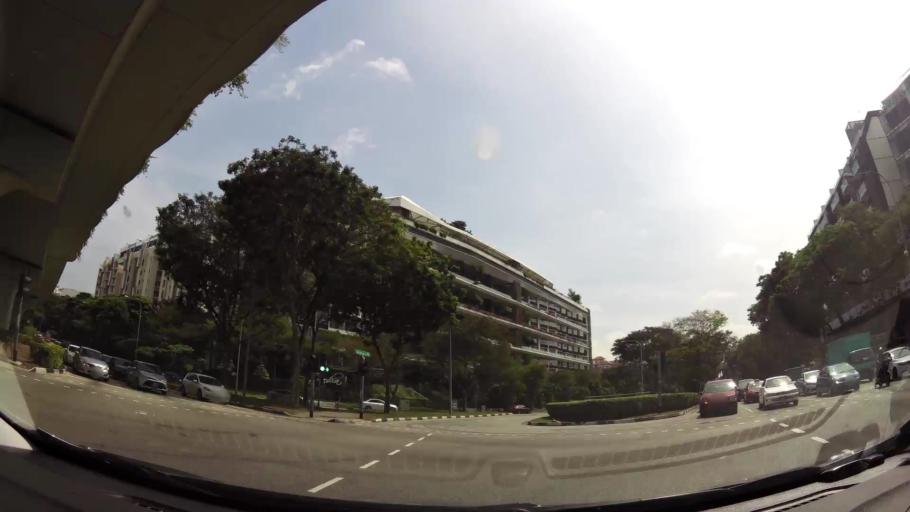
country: SG
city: Singapore
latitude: 1.3376
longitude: 103.7789
